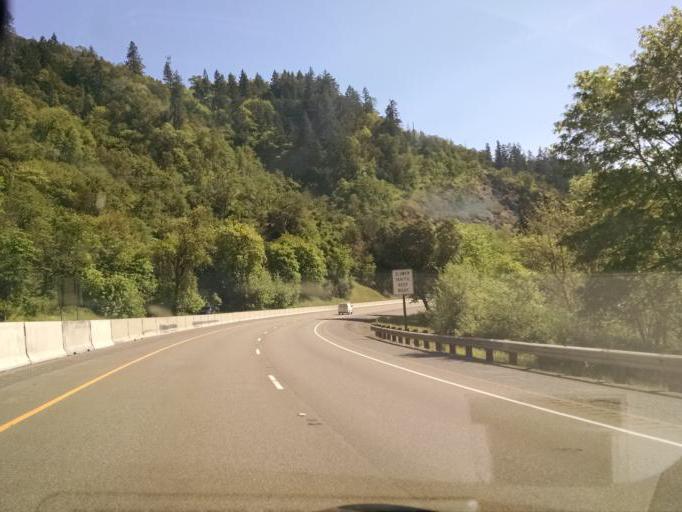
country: US
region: Oregon
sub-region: Douglas County
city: Tri-City
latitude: 42.9606
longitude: -123.3251
